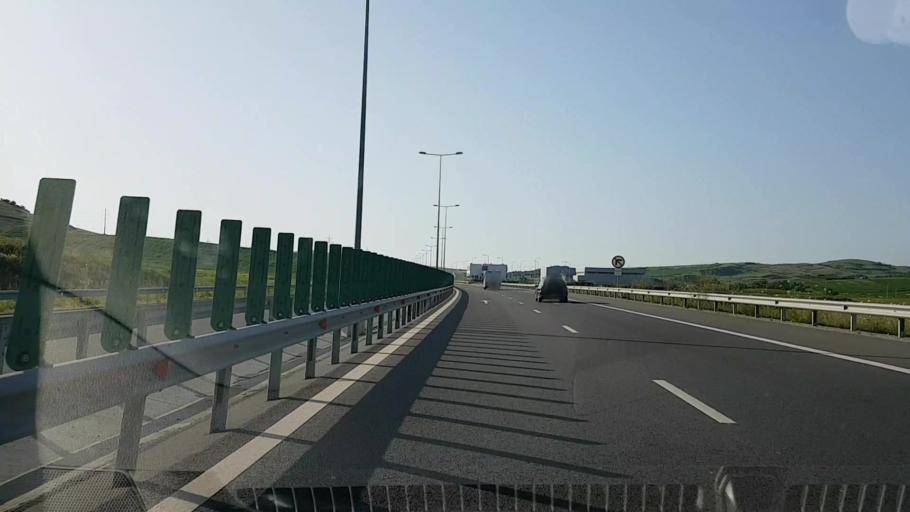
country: RO
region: Alba
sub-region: Comuna Unirea
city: Unirea
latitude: 46.4477
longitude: 23.7958
